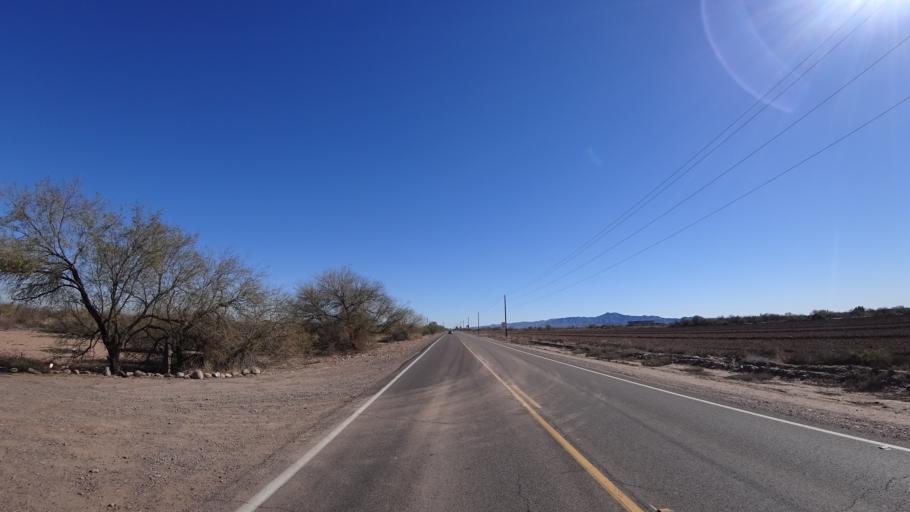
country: US
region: Arizona
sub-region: Maricopa County
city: Tolleson
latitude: 33.3773
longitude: -112.2453
